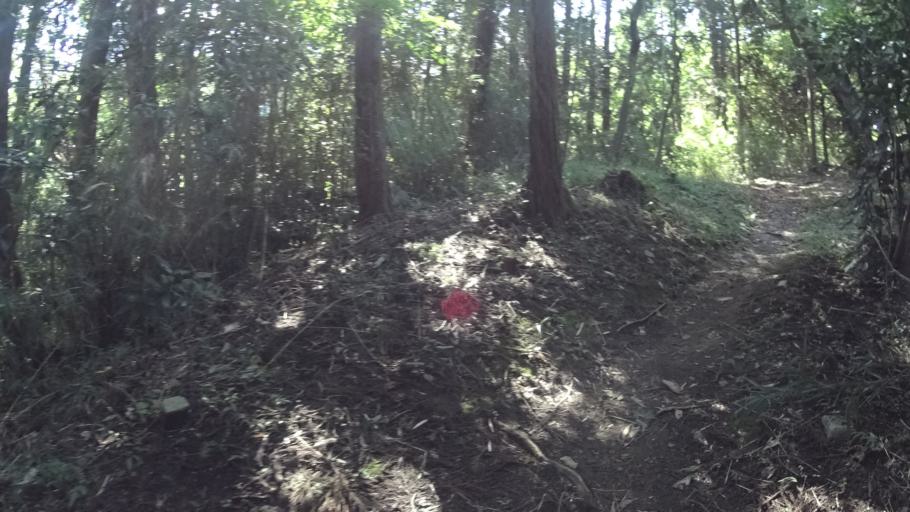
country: JP
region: Kanagawa
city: Kamakura
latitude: 35.3607
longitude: 139.5864
